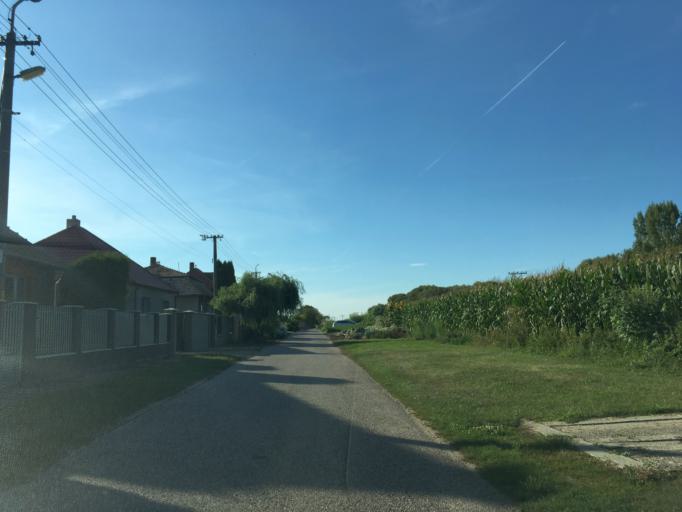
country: SK
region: Nitriansky
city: Svodin
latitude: 47.8989
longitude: 18.4161
